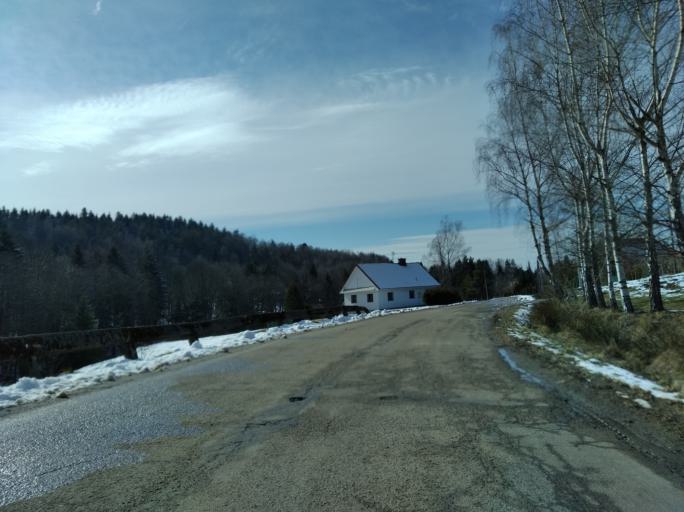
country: PL
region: Subcarpathian Voivodeship
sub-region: Powiat krosnienski
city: Korczyna
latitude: 49.7459
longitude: 21.8111
